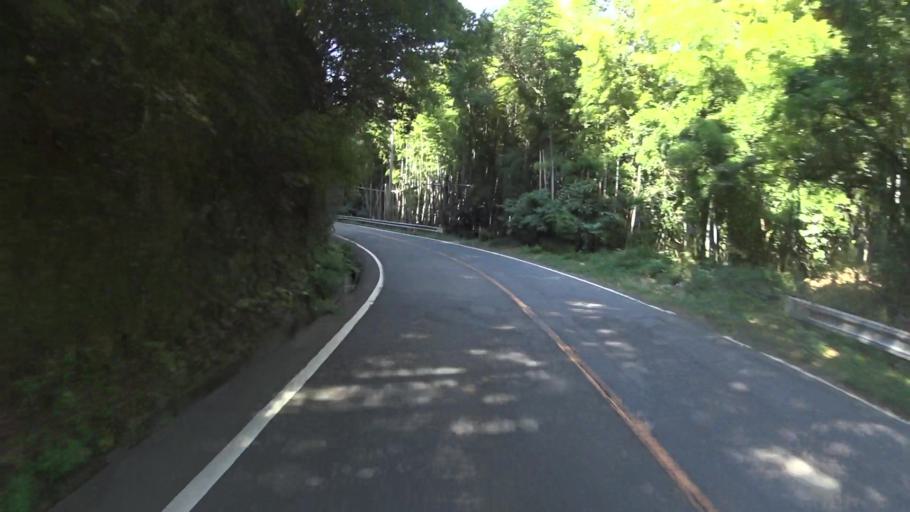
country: JP
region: Kyoto
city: Kameoka
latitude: 34.9848
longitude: 135.5371
